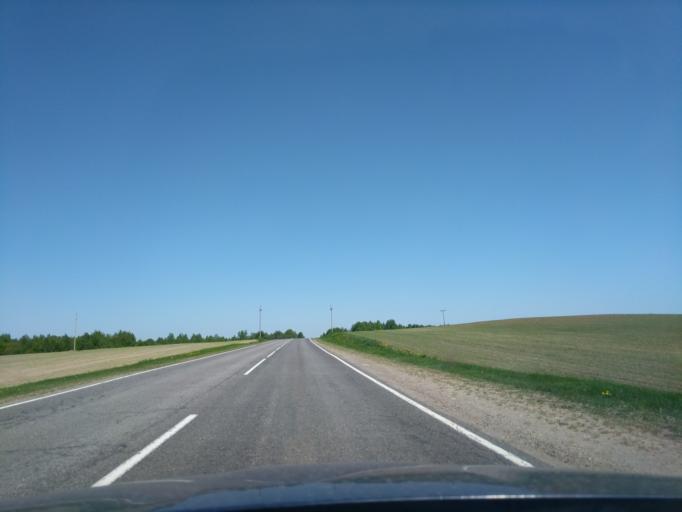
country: BY
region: Minsk
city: Il'ya
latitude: 54.3006
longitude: 27.4774
